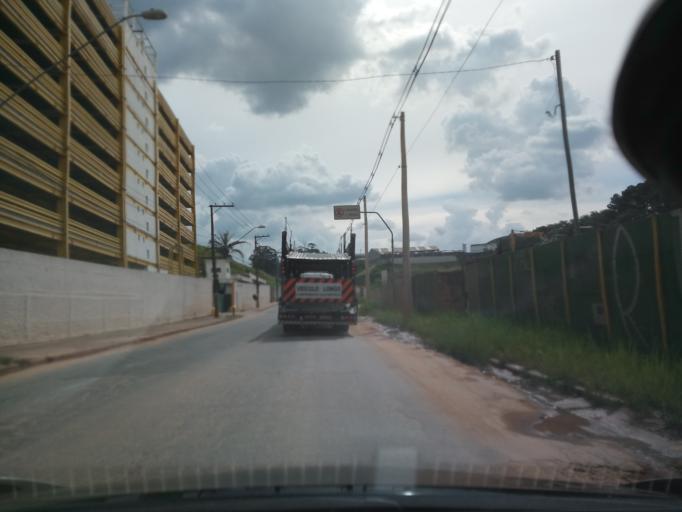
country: BR
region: Sao Paulo
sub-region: Sao Bernardo Do Campo
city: Sao Bernardo do Campo
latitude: -23.7408
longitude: -46.5604
